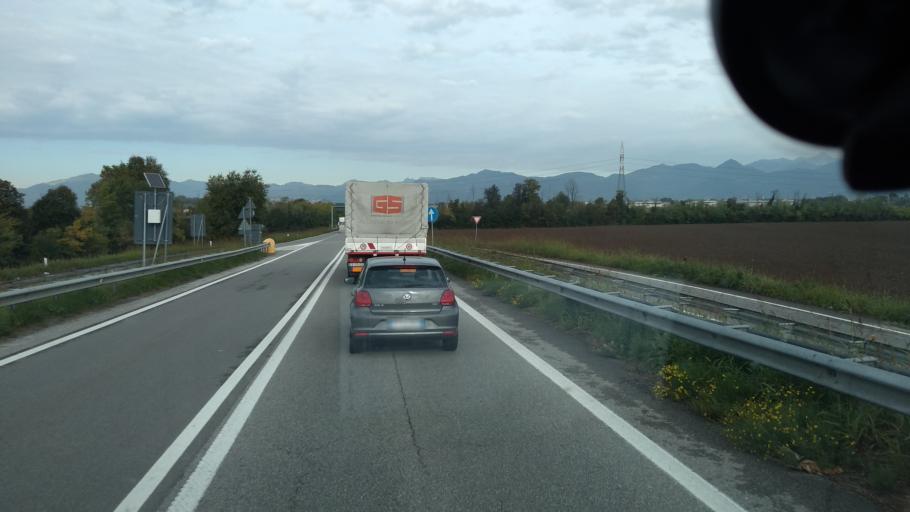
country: IT
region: Lombardy
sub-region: Provincia di Bergamo
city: Grassobbio
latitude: 45.6375
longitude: 9.7127
